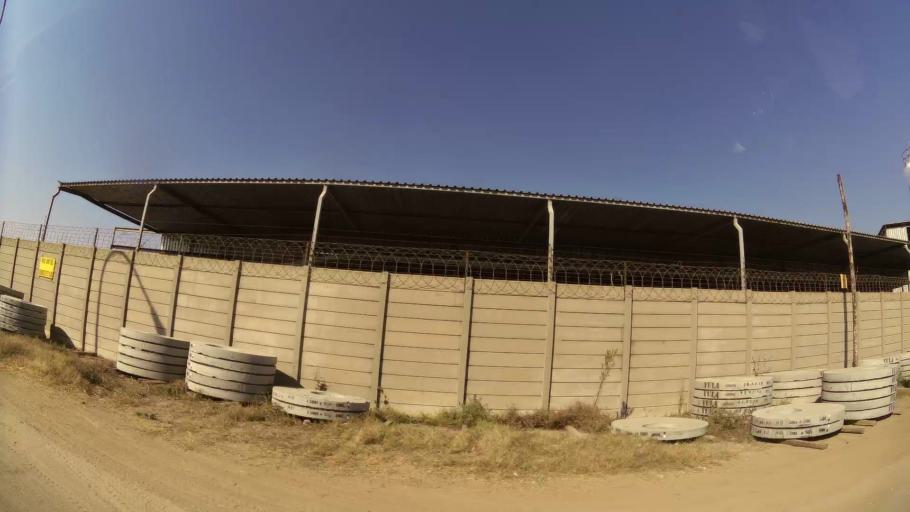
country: ZA
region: Gauteng
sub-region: Ekurhuleni Metropolitan Municipality
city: Benoni
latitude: -26.2026
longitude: 28.3135
